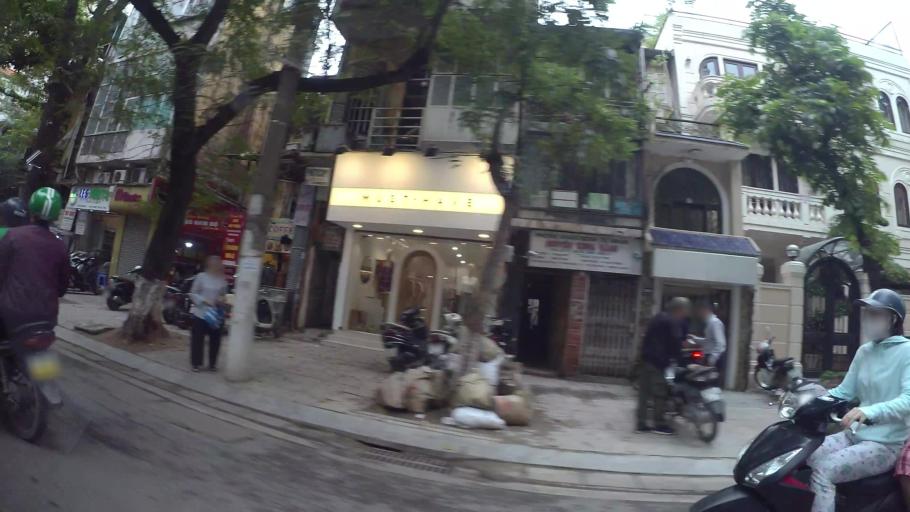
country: VN
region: Ha Noi
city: Hai BaTrung
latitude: 21.0157
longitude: 105.8492
